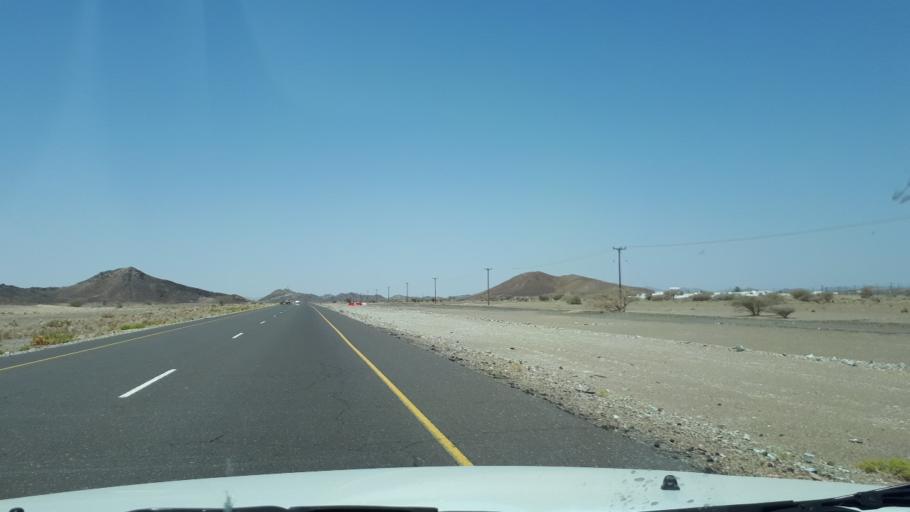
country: OM
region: Ash Sharqiyah
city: Ibra'
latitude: 22.6373
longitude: 58.4762
